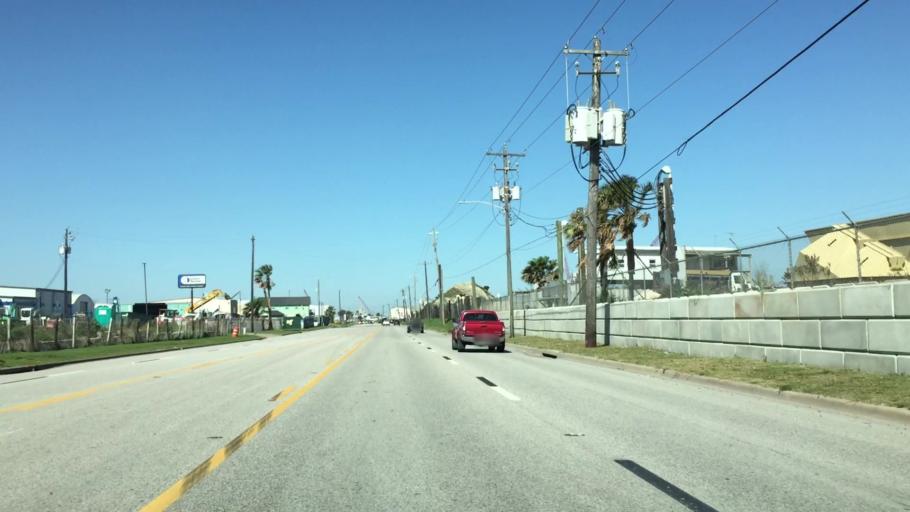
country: US
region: Texas
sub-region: Galveston County
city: Galveston
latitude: 29.2969
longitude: -94.8441
